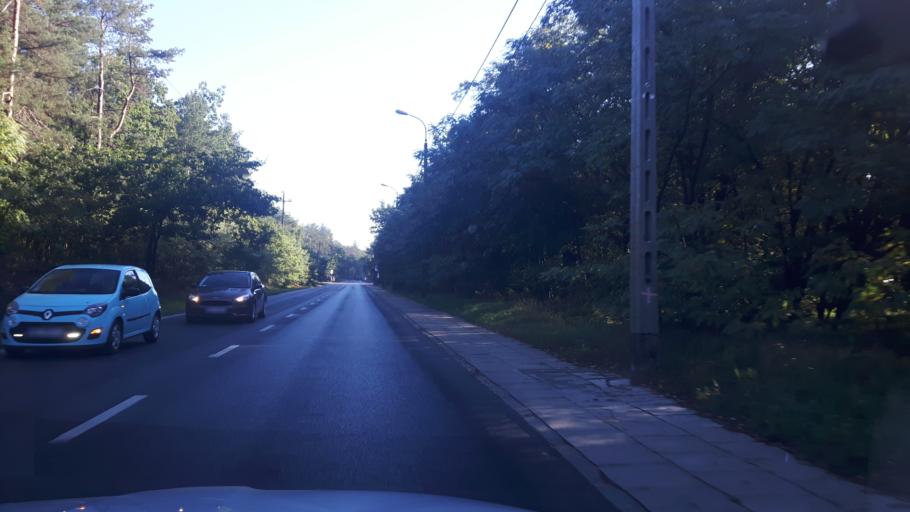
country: PL
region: Masovian Voivodeship
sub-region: Warszawa
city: Bialoleka
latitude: 52.3443
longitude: 20.9956
